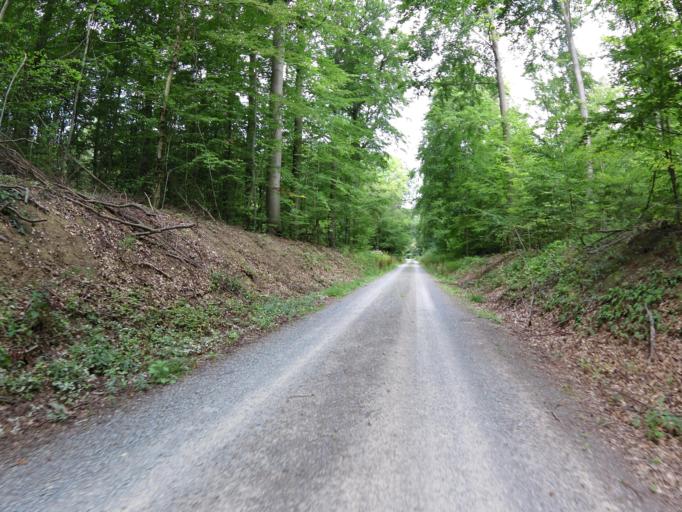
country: DE
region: Bavaria
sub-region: Regierungsbezirk Unterfranken
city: Kist
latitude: 49.7257
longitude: 9.8293
